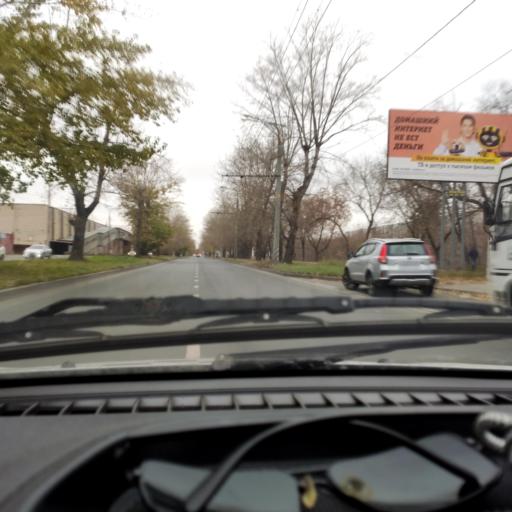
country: RU
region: Samara
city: Tol'yatti
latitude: 53.5154
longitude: 49.4389
